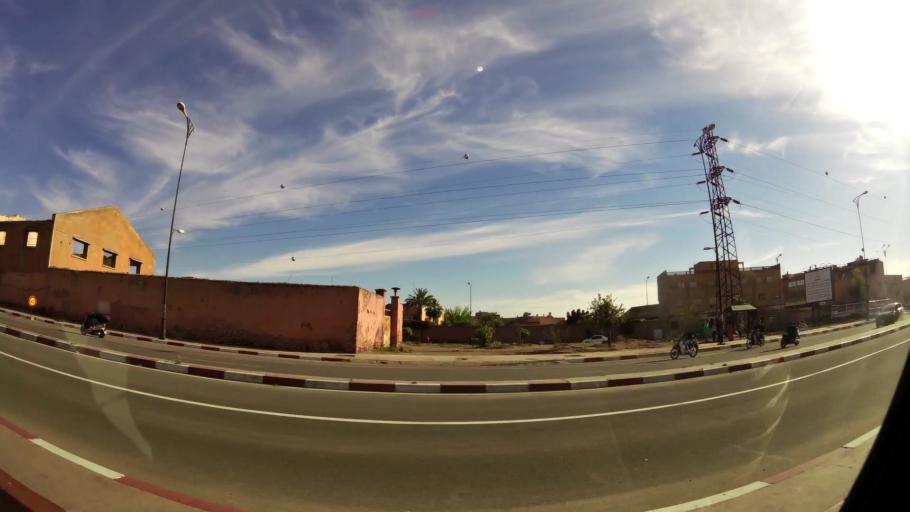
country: MA
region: Marrakech-Tensift-Al Haouz
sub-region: Marrakech
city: Marrakesh
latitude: 31.6274
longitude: -8.0362
